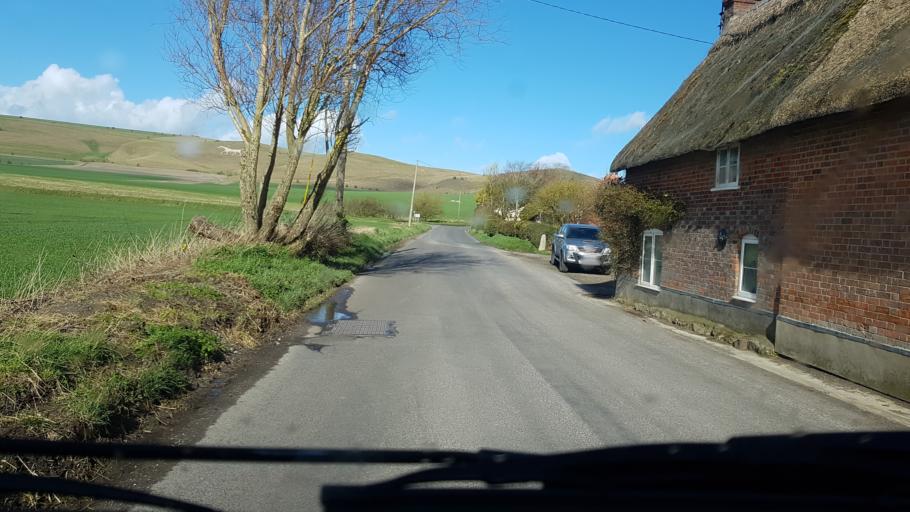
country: GB
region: England
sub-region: Wiltshire
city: Woodborough
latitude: 51.3591
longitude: -1.8499
